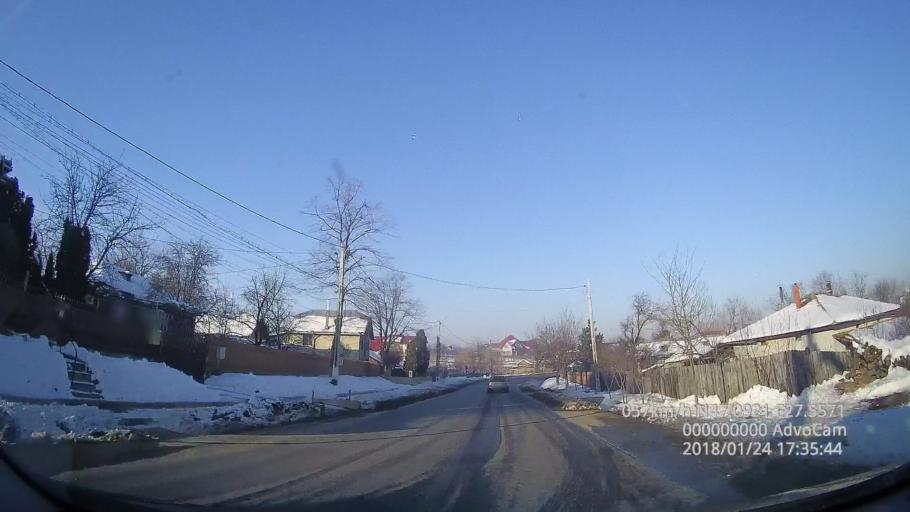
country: RO
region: Iasi
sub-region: Comuna Ciurea
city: Lunca Cetatuii
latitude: 47.0925
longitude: 27.5572
